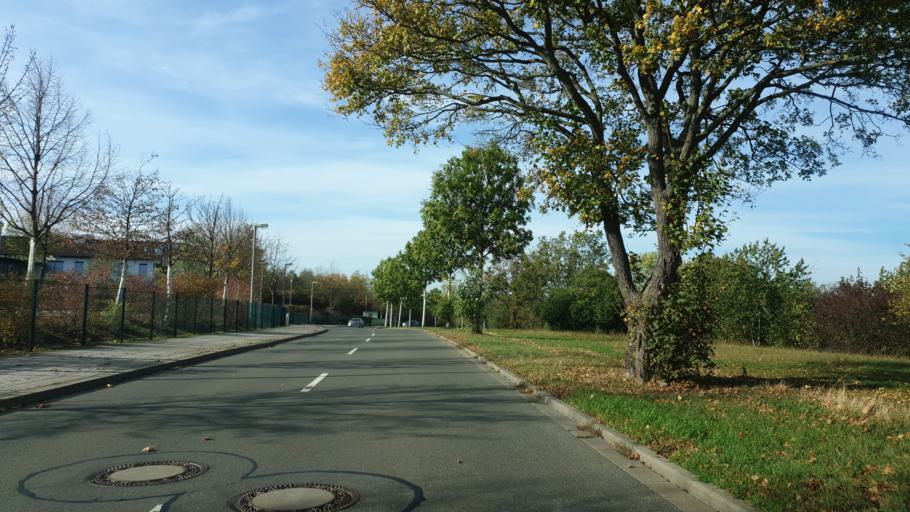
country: DE
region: Thuringia
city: Schwaara
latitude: 50.9050
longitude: 12.1119
